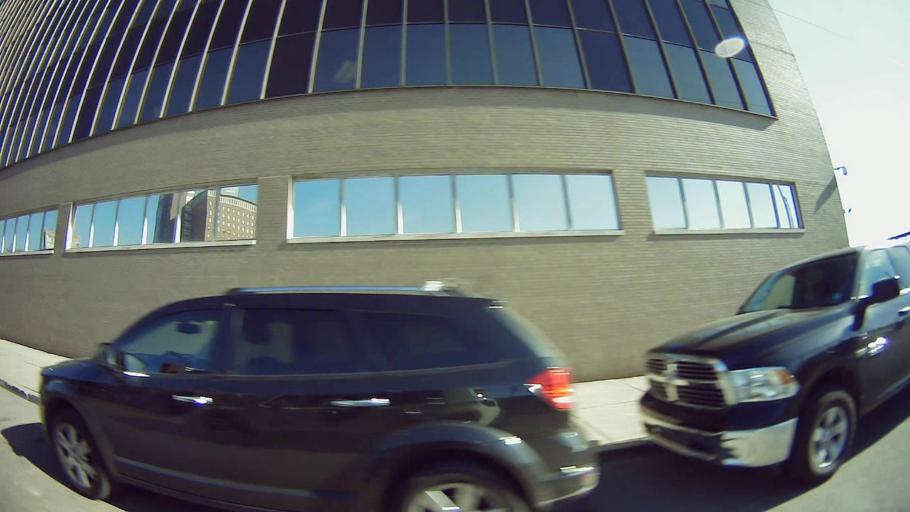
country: US
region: Michigan
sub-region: Wayne County
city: Highland Park
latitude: 42.3648
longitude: -83.0830
